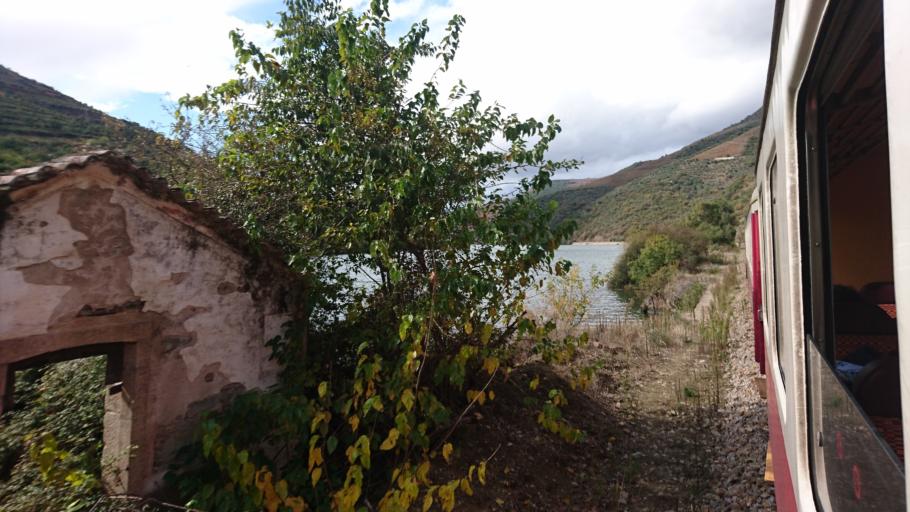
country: PT
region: Viseu
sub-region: Armamar
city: Armamar
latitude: 41.1636
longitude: -7.6592
